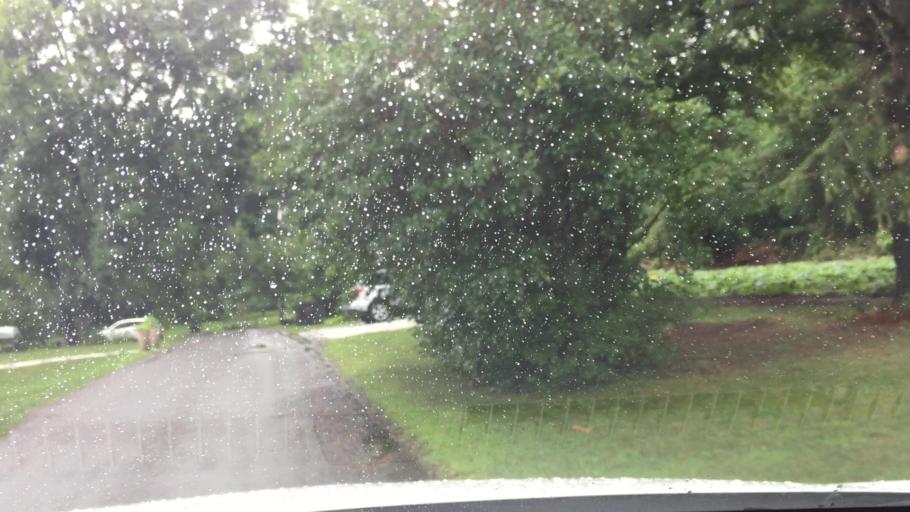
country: US
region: Massachusetts
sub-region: Berkshire County
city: Lenox
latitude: 42.4106
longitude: -73.3144
